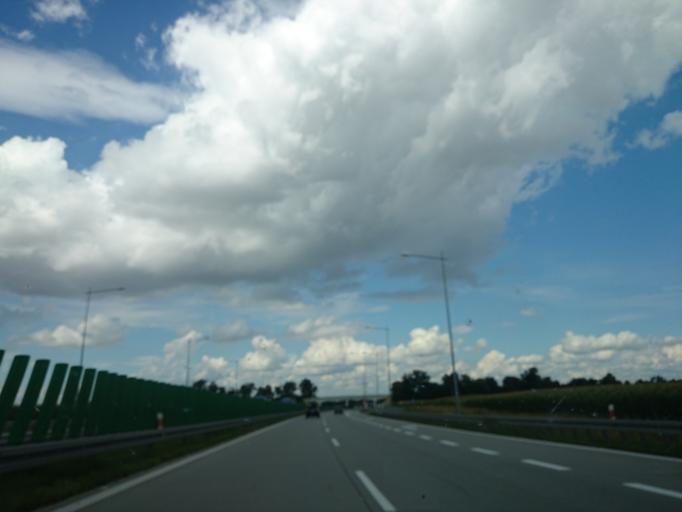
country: PL
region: Lower Silesian Voivodeship
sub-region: Powiat sredzki
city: Udanin
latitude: 51.0844
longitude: 16.4222
